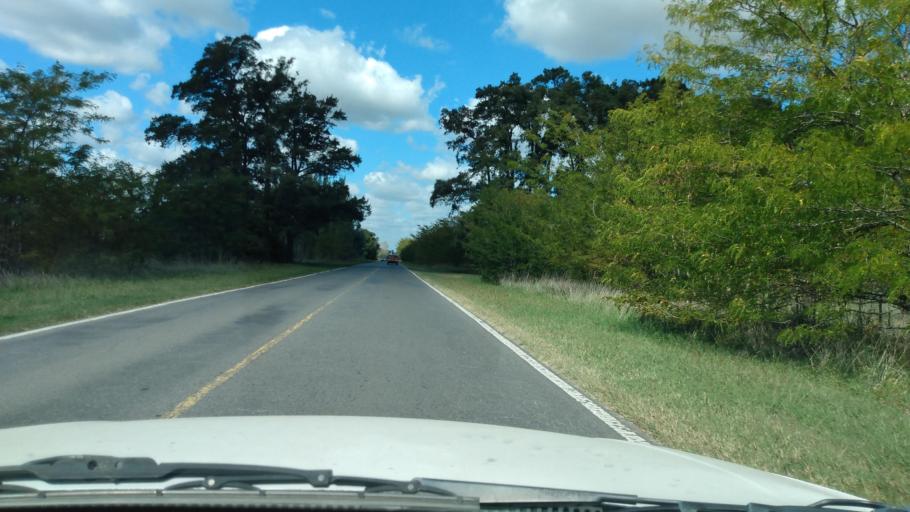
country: AR
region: Buenos Aires
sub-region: Partido de Navarro
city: Navarro
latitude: -34.9344
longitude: -59.3232
